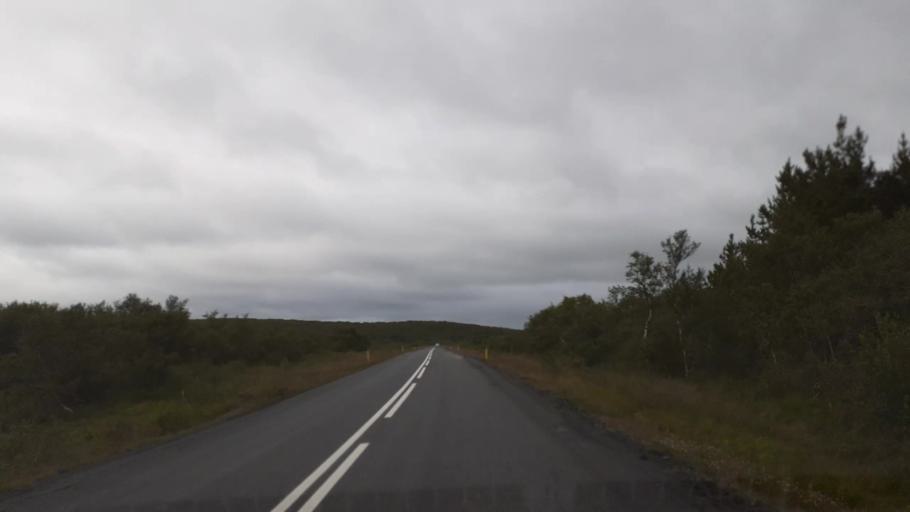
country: IS
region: Northeast
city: Husavik
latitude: 66.0464
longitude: -16.4401
